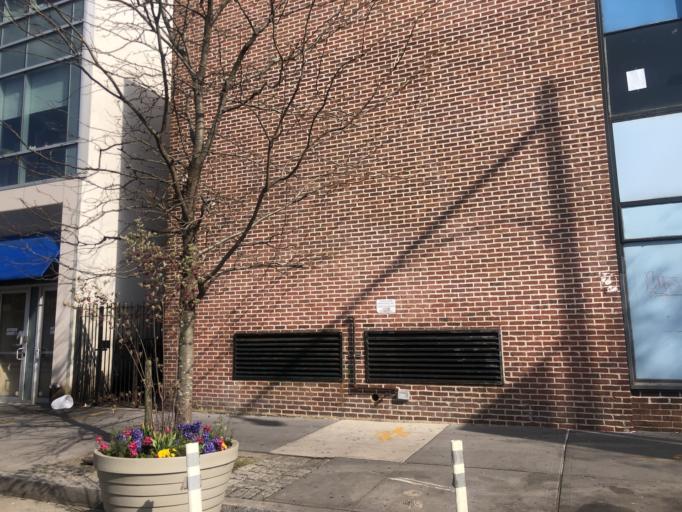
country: US
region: New York
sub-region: Kings County
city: Brooklyn
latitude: 40.6323
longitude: -73.9485
